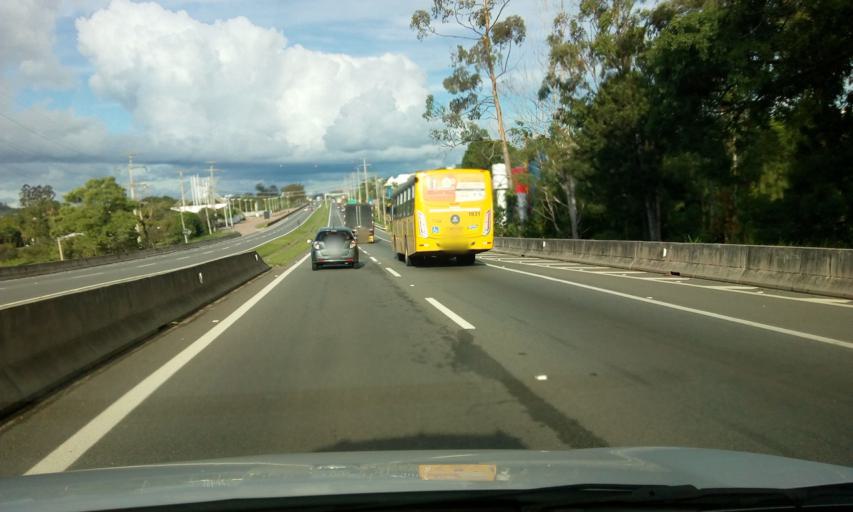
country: BR
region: Sao Paulo
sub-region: Jundiai
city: Jundiai
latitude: -23.1563
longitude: -46.8910
